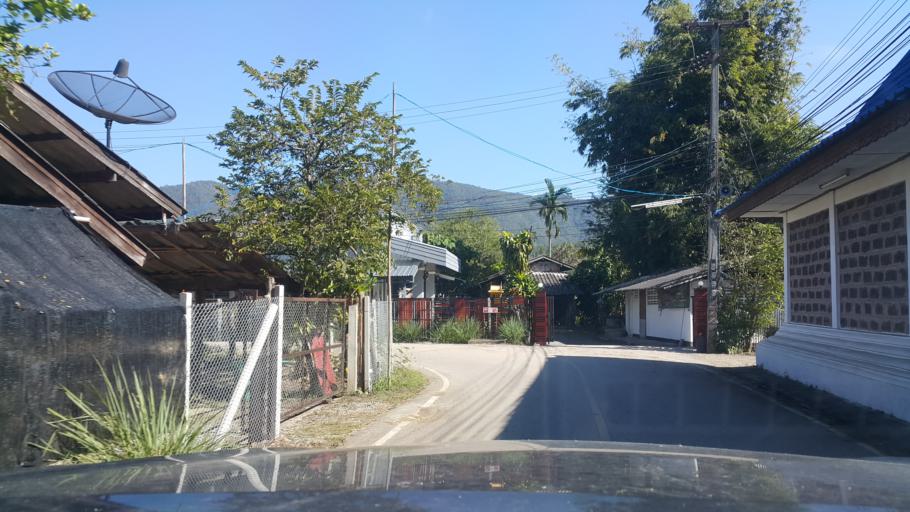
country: TH
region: Chiang Mai
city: Mae On
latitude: 18.7826
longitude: 99.2603
